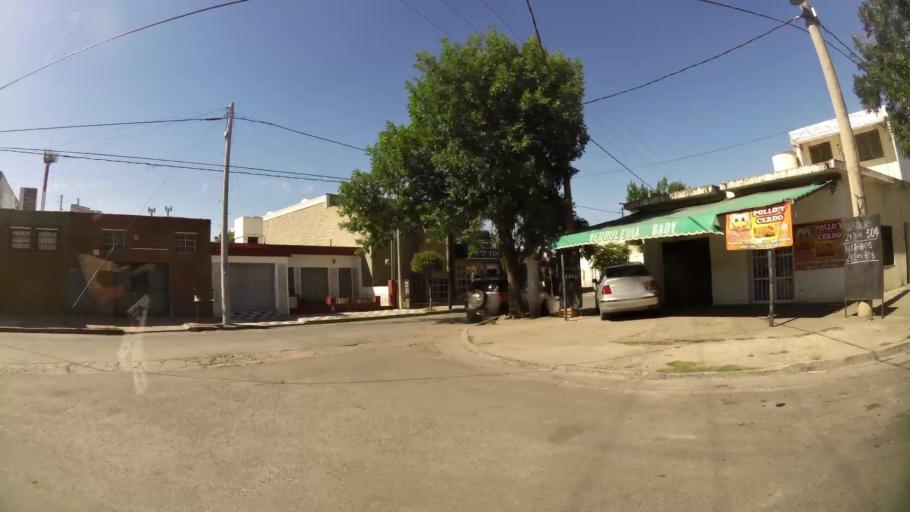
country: AR
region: Cordoba
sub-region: Departamento de Capital
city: Cordoba
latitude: -31.3746
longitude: -64.1714
